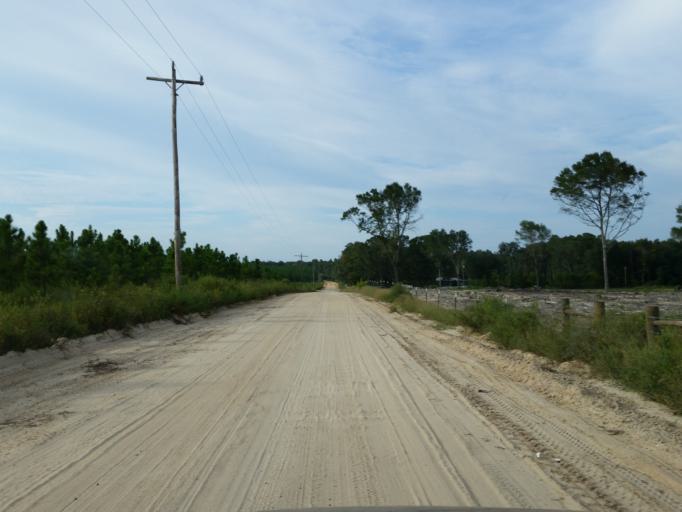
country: US
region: Florida
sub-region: Madison County
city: Madison
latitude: 30.5349
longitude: -83.2158
